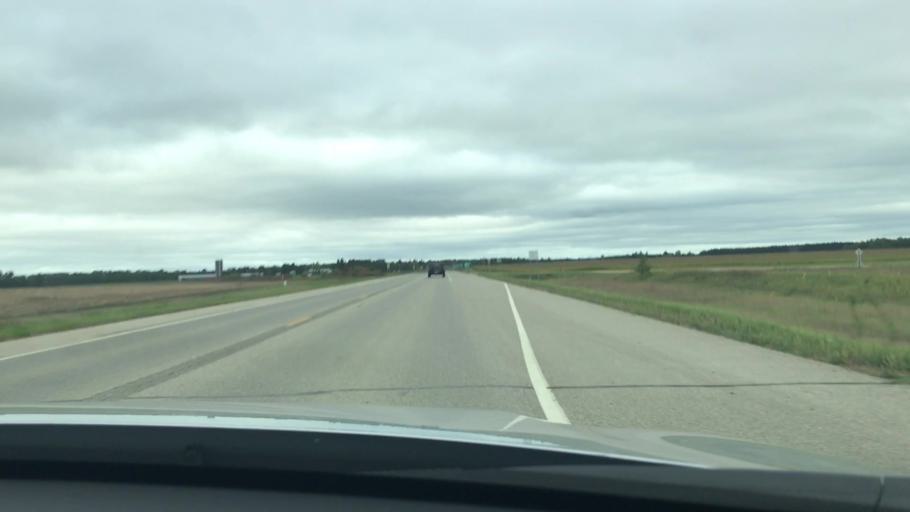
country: US
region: Minnesota
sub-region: Hubbard County
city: Park Rapids
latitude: 46.8556
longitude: -95.0755
